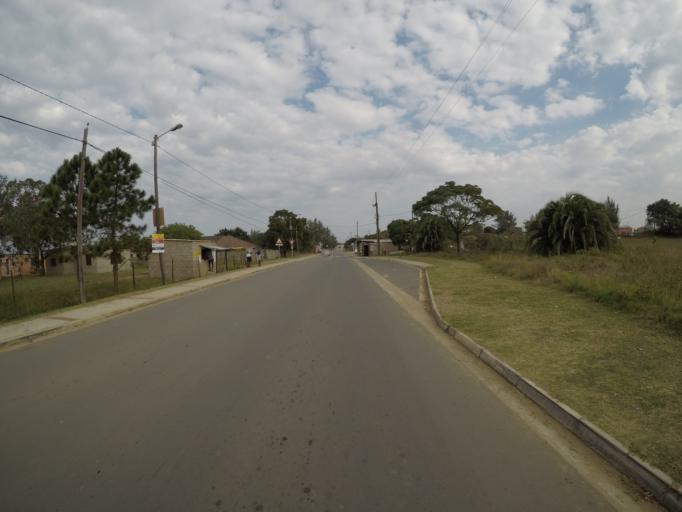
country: ZA
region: KwaZulu-Natal
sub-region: uThungulu District Municipality
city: Richards Bay
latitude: -28.7388
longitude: 32.1008
